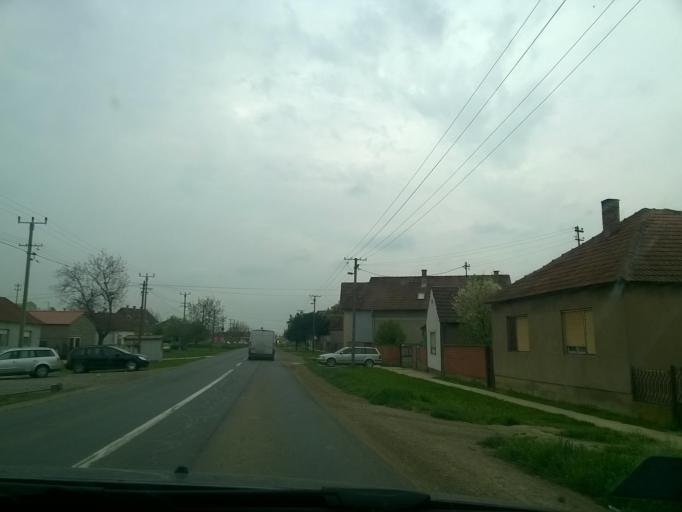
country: RS
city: Platicevo
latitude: 44.8285
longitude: 19.7779
